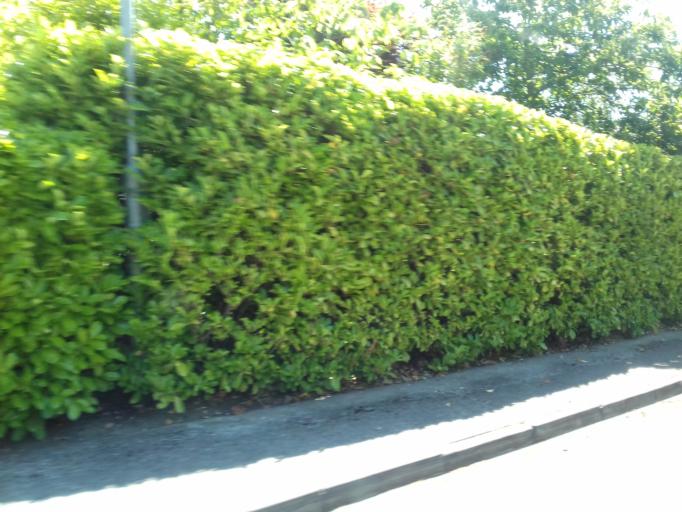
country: IE
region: Leinster
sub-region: Fingal County
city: Swords
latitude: 53.4852
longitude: -6.2713
